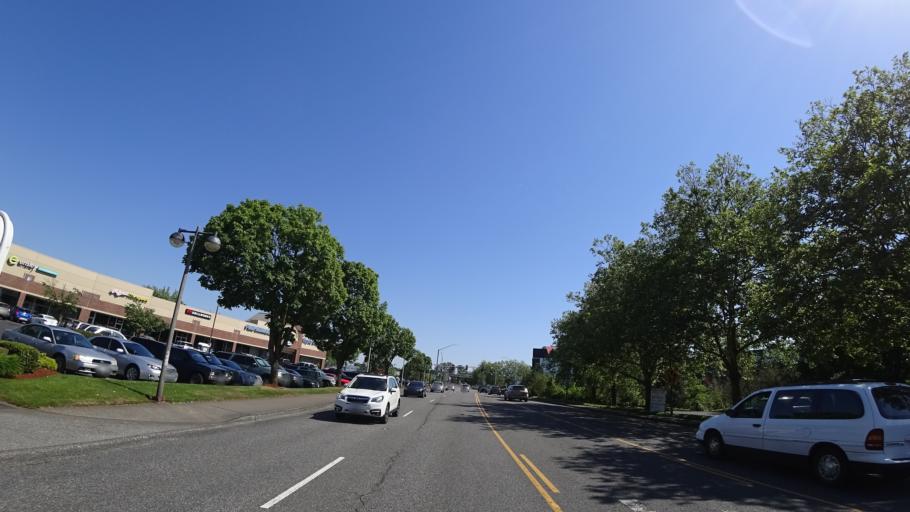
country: US
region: Oregon
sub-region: Washington County
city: Beaverton
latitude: 45.4922
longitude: -122.8062
